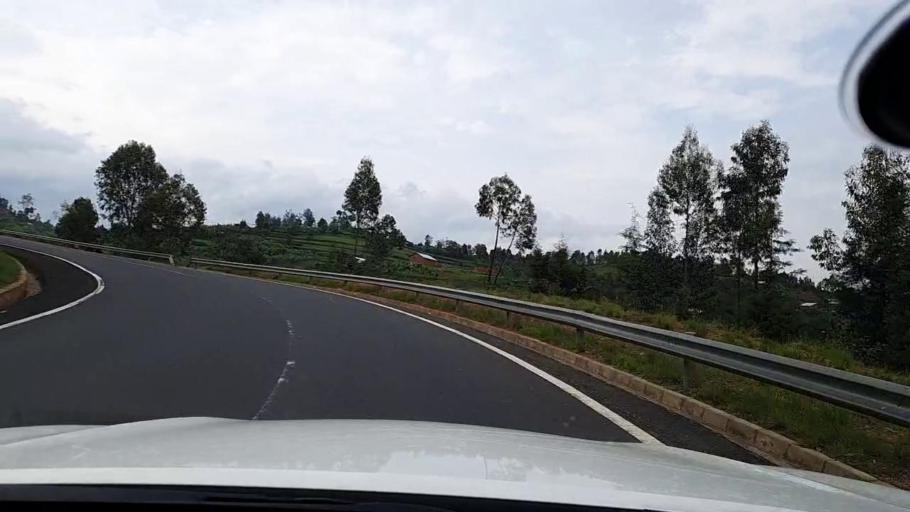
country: RW
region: Western Province
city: Kibuye
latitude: -2.1689
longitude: 29.2894
